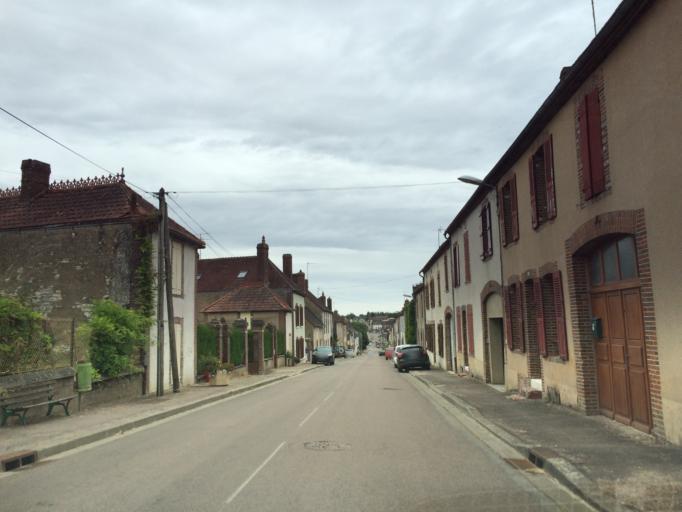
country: FR
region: Bourgogne
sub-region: Departement de l'Yonne
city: Aillant-sur-Tholon
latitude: 47.8732
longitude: 3.3433
